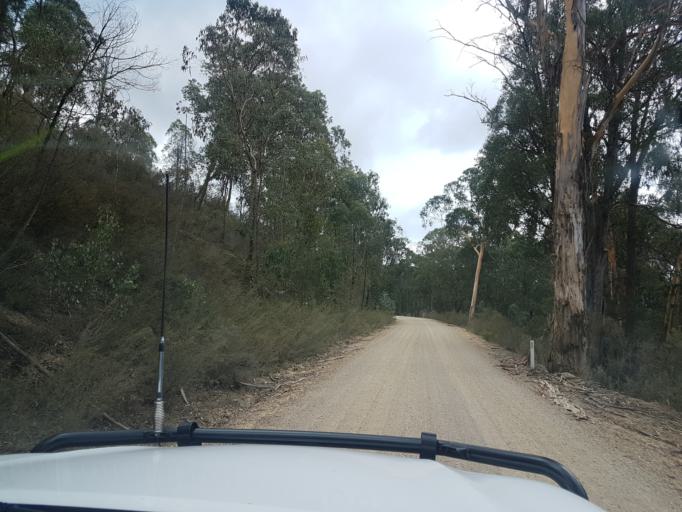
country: AU
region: Victoria
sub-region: East Gippsland
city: Bairnsdale
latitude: -37.6955
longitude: 147.5651
